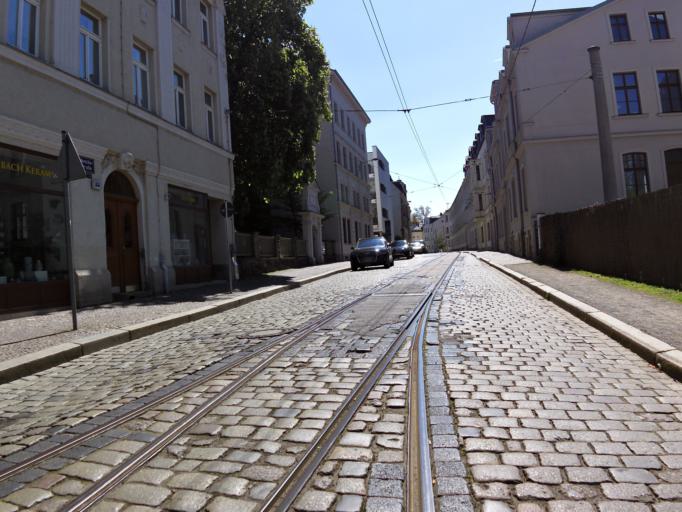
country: DE
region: Saxony
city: Leipzig
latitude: 51.3590
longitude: 12.3625
